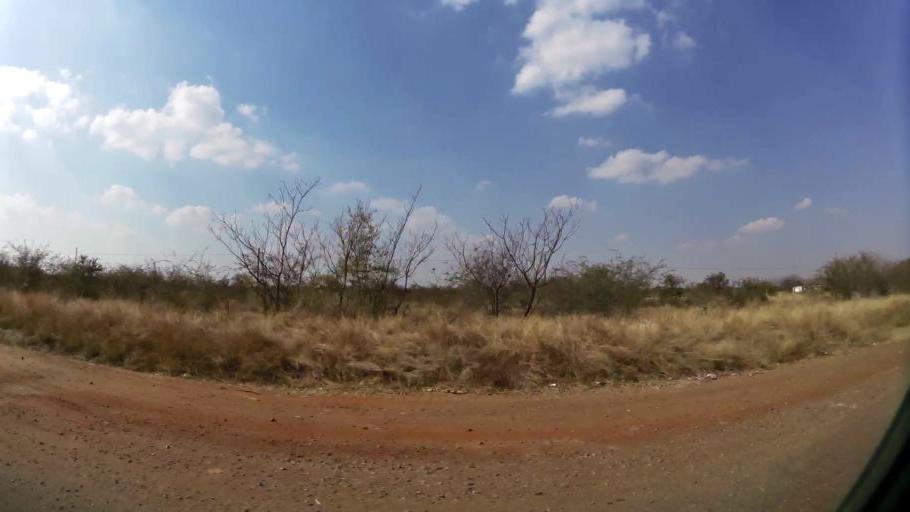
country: ZA
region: North-West
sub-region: Bojanala Platinum District Municipality
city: Rustenburg
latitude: -25.5068
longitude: 27.0991
